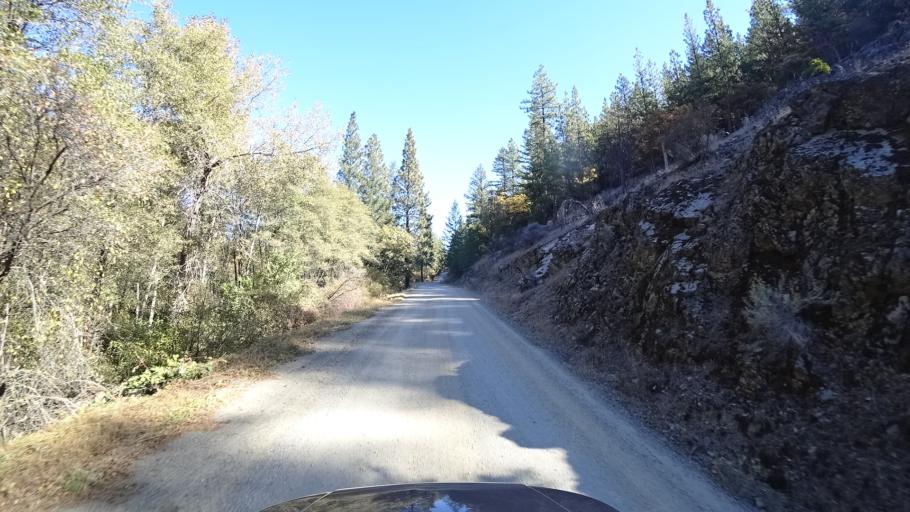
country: US
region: California
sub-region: Siskiyou County
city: Weed
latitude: 41.2958
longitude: -122.8072
